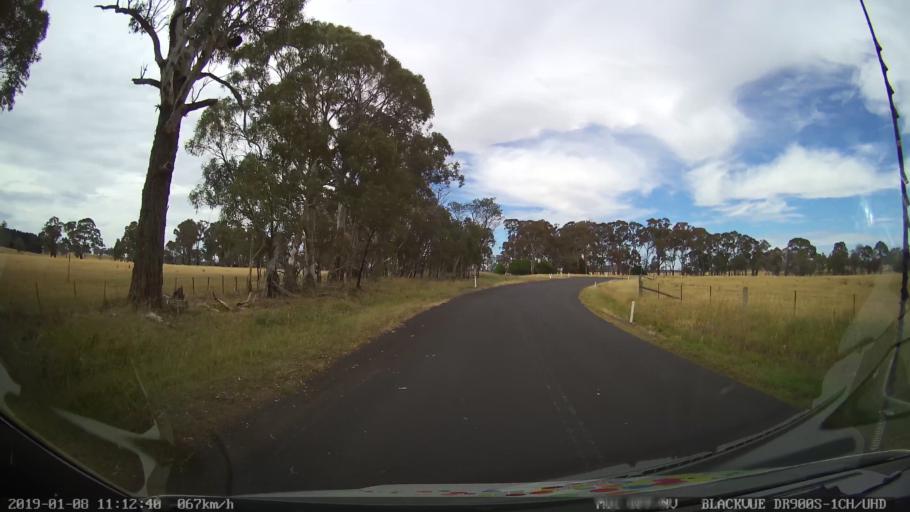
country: AU
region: New South Wales
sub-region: Guyra
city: Guyra
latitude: -30.2297
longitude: 151.6096
